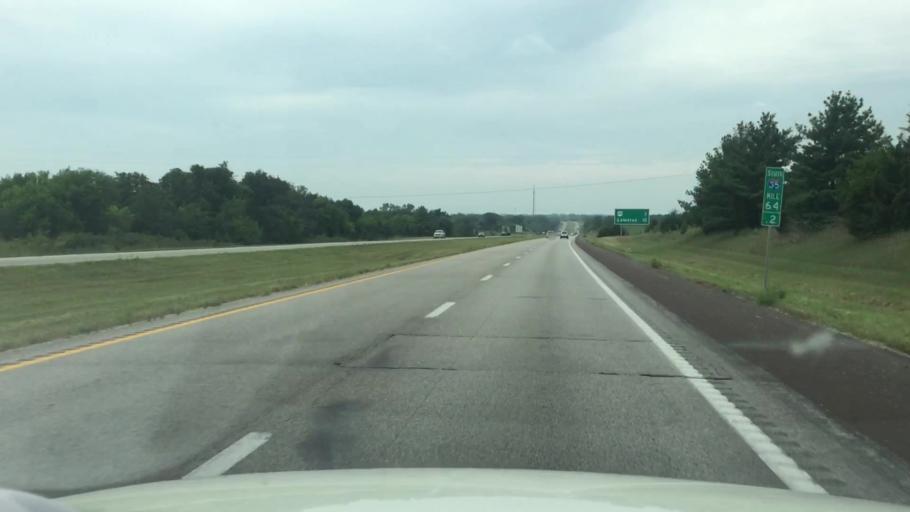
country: US
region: Missouri
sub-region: Clinton County
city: Cameron
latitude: 39.8898
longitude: -94.1570
